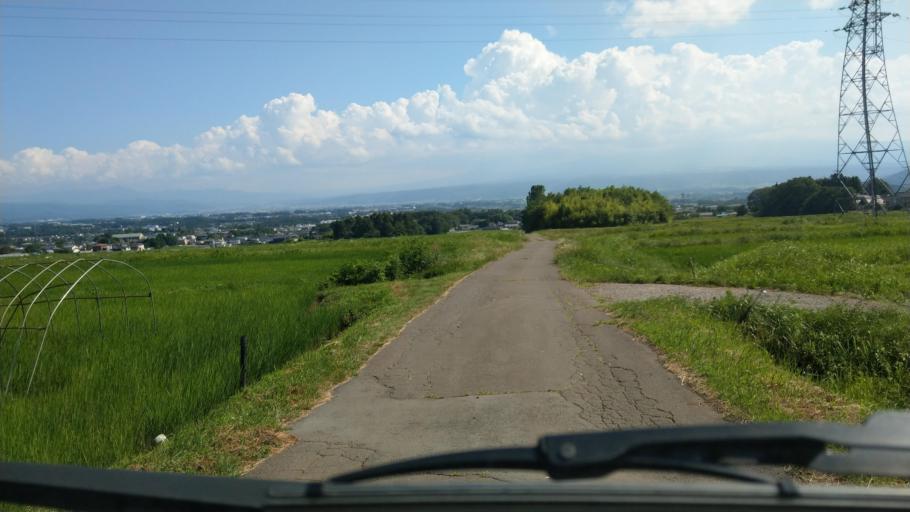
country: JP
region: Nagano
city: Komoro
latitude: 36.3292
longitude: 138.4510
